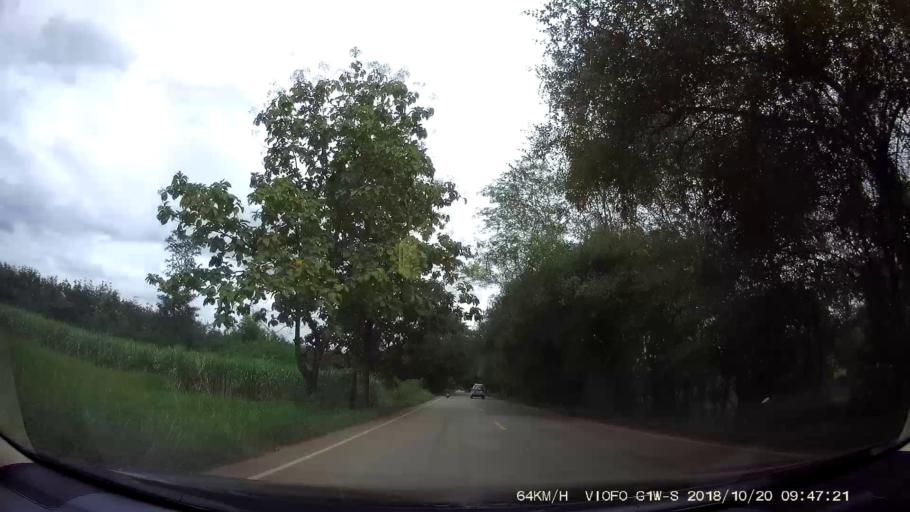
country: TH
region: Chaiyaphum
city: Khon San
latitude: 16.5030
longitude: 101.9202
